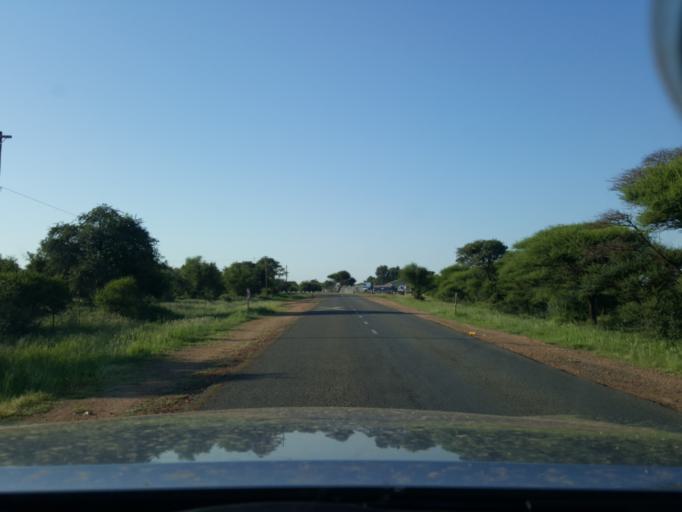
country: ZA
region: North-West
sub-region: Ngaka Modiri Molema District Municipality
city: Mmabatho
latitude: -25.6444
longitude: 25.5742
